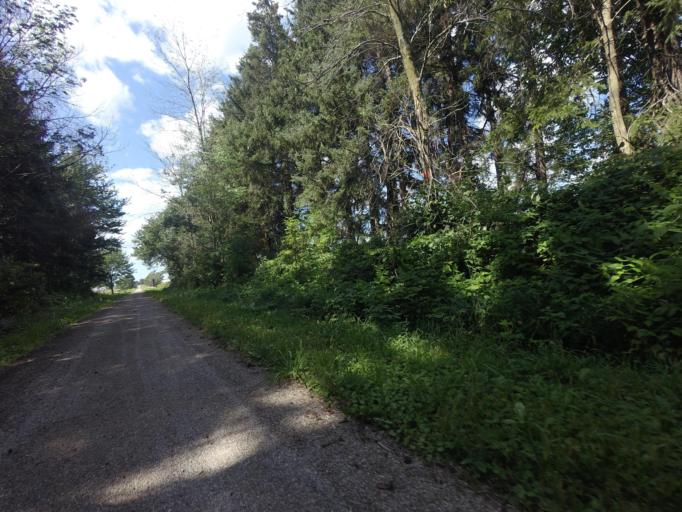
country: CA
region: Ontario
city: Huron East
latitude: 43.6609
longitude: -81.2527
